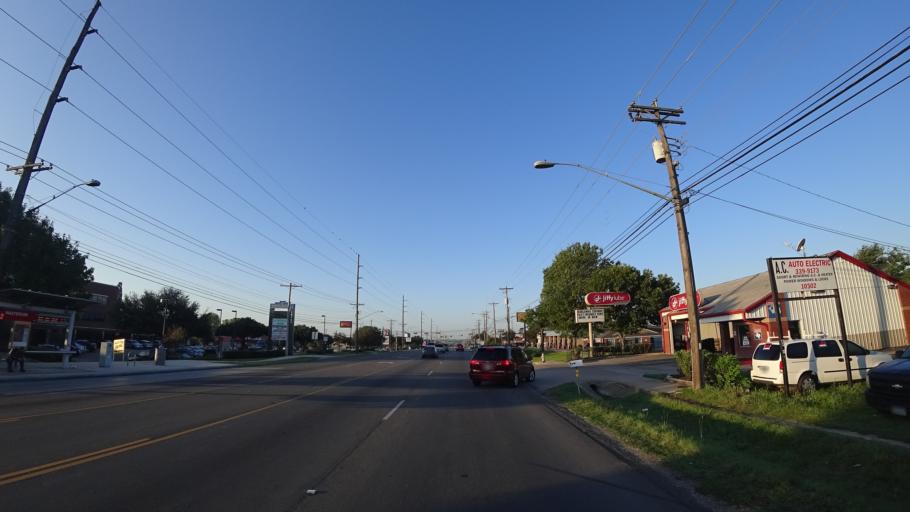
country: US
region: Texas
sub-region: Travis County
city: Wells Branch
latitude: 30.3722
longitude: -97.6919
